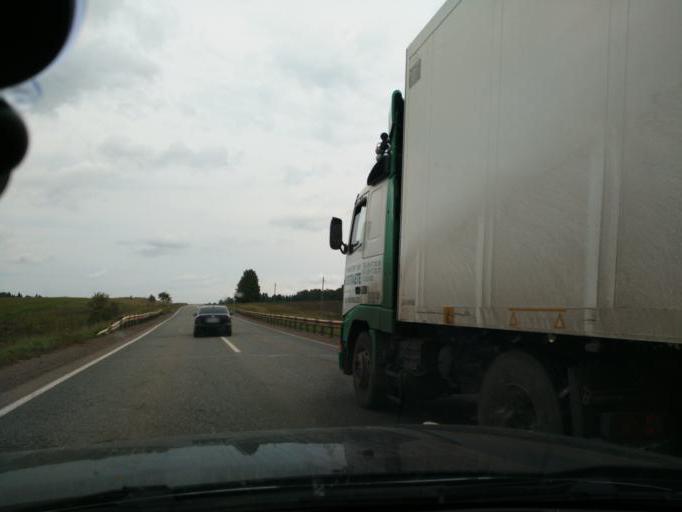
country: RU
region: Perm
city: Kuyeda
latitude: 56.4660
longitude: 55.6706
